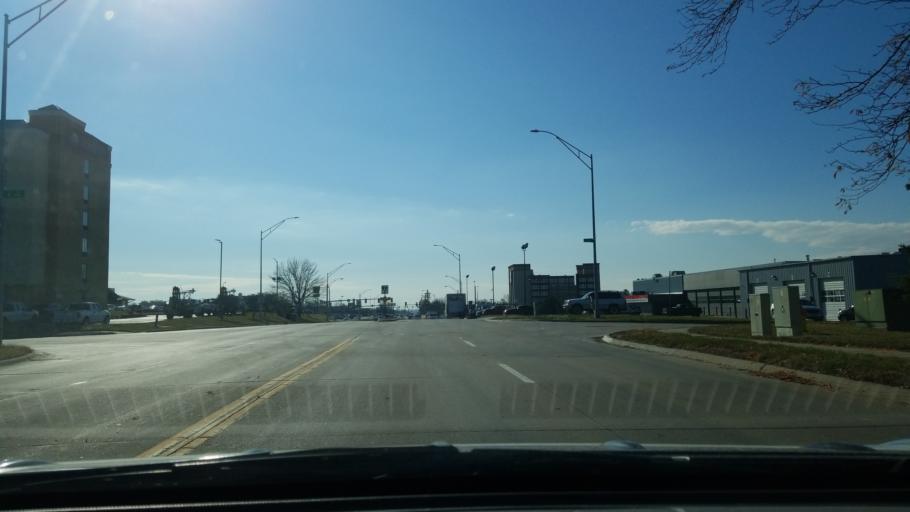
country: US
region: Nebraska
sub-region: Douglas County
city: Ralston
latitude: 41.2146
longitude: -96.0816
